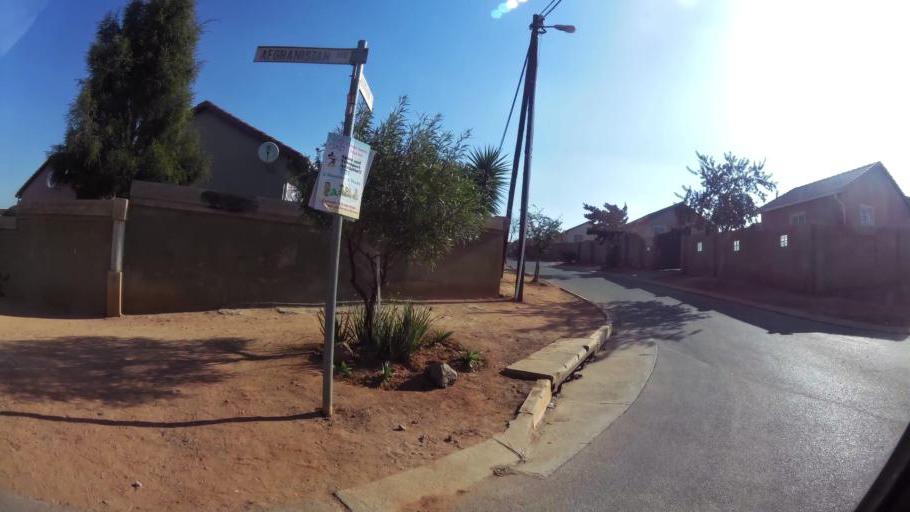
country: ZA
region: Gauteng
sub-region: West Rand District Municipality
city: Muldersdriseloop
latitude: -26.0356
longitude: 27.9150
